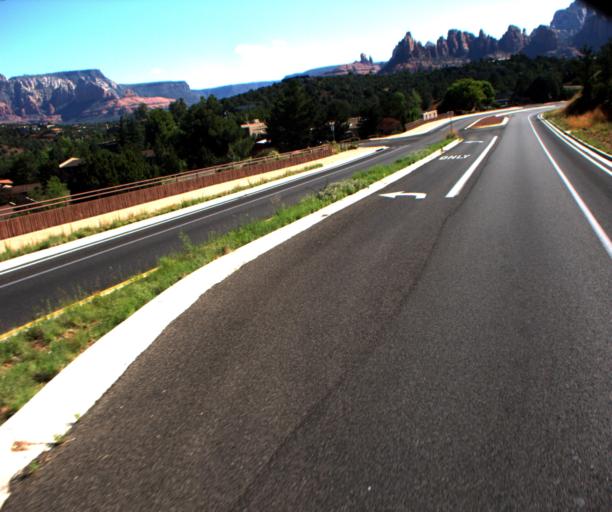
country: US
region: Arizona
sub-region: Coconino County
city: Sedona
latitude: 34.8430
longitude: -111.7749
